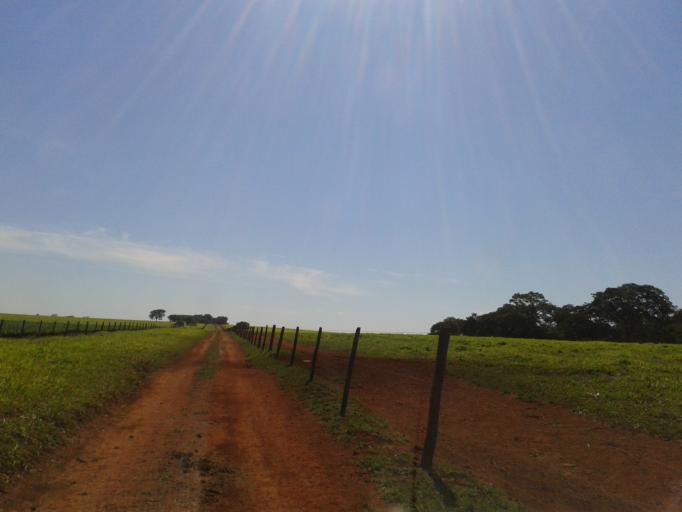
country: BR
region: Minas Gerais
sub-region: Centralina
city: Centralina
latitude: -18.6525
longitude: -49.2806
